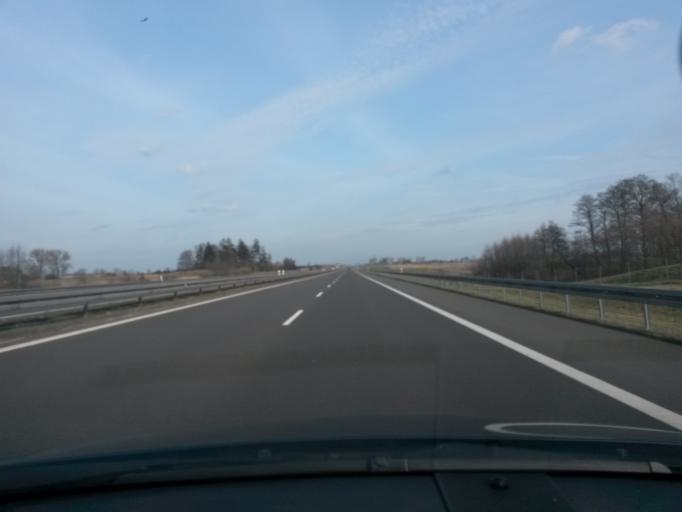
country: PL
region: Greater Poland Voivodeship
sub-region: Powiat wrzesinski
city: Wrzesnia
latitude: 52.3183
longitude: 17.4869
